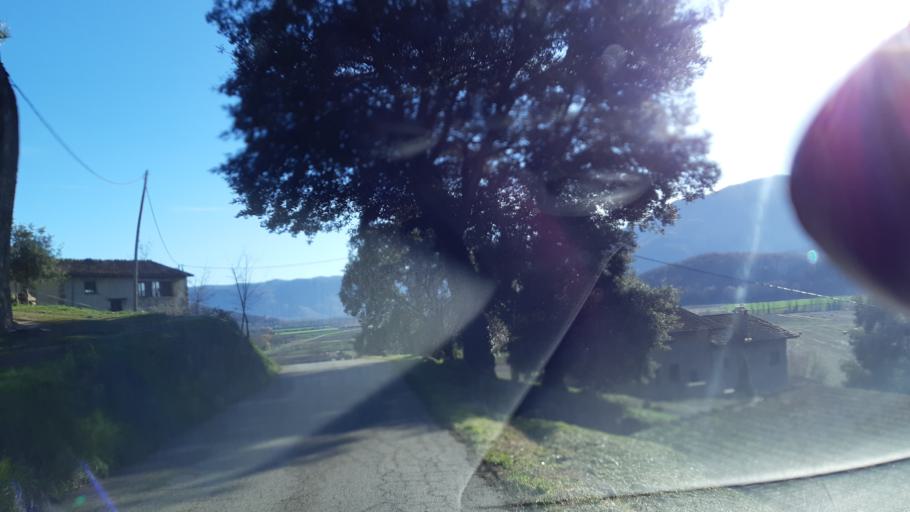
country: ES
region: Catalonia
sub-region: Provincia de Girona
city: Bas
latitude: 42.1493
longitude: 2.4376
